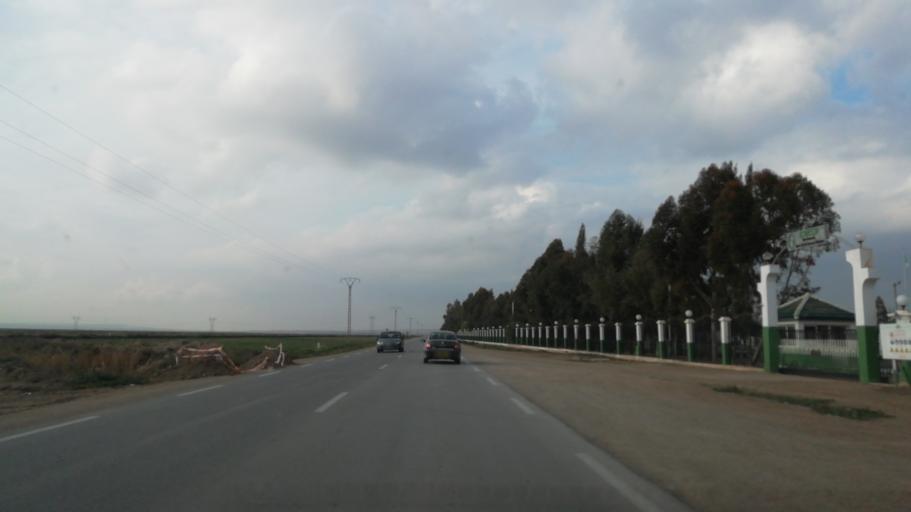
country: DZ
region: Mascara
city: Sig
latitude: 35.6942
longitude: -0.0205
